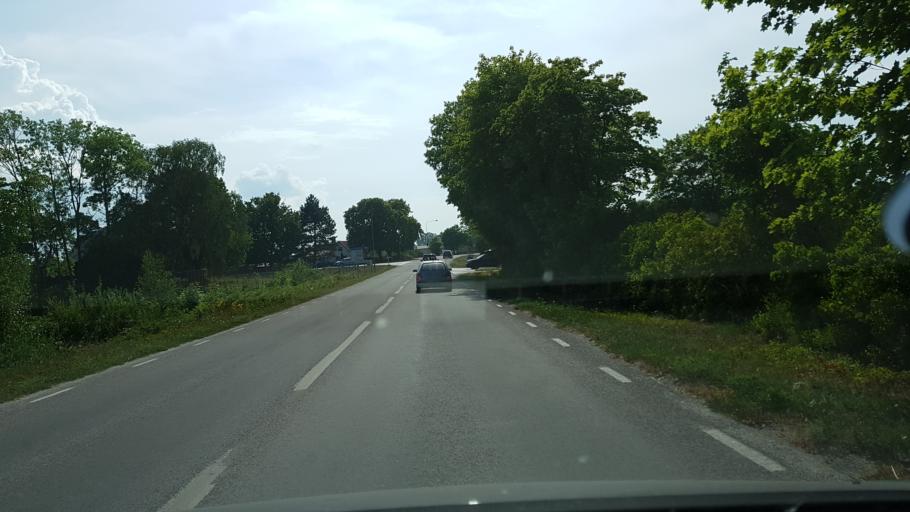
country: SE
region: Gotland
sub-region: Gotland
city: Visby
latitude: 57.8005
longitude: 18.5157
